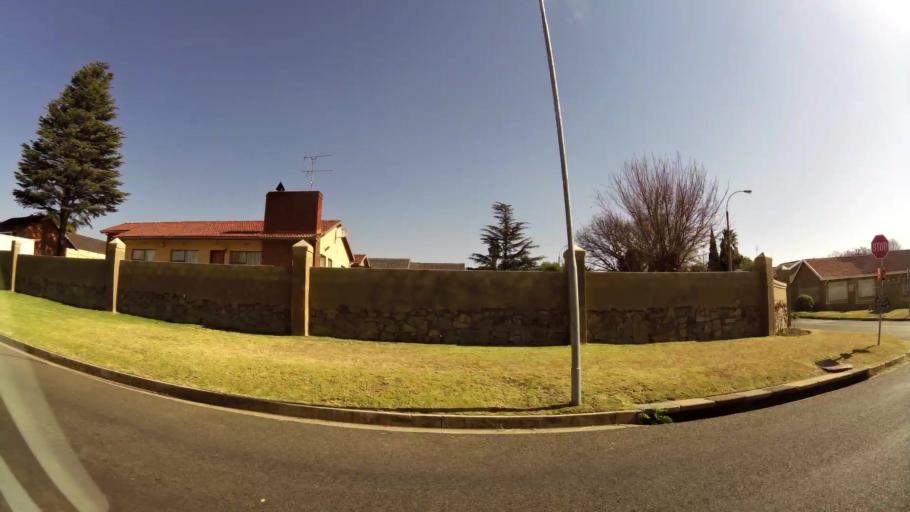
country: ZA
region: Gauteng
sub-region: City of Johannesburg Metropolitan Municipality
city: Modderfontein
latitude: -26.0539
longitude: 28.2123
